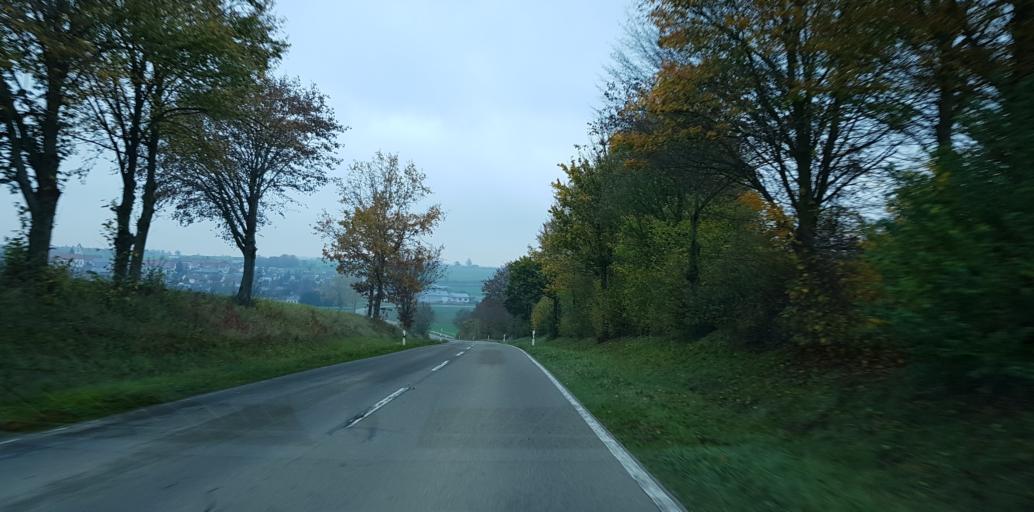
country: DE
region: Baden-Wuerttemberg
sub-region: Tuebingen Region
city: Altheim
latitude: 48.3195
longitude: 9.7744
